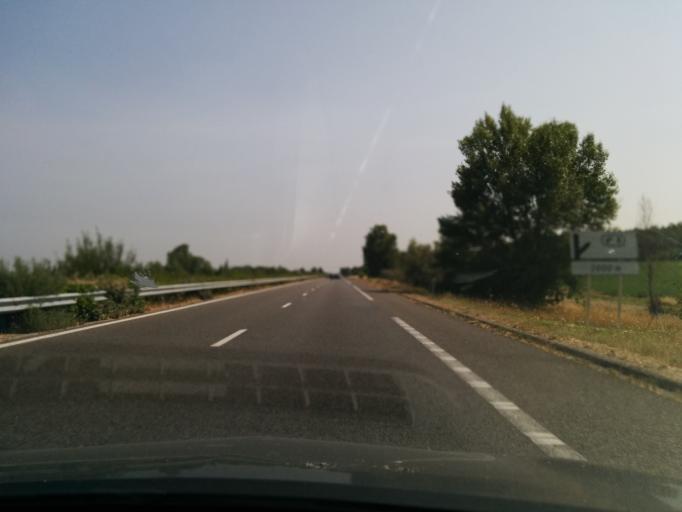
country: FR
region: Midi-Pyrenees
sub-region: Departement du Tarn
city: Lisle-sur-Tarn
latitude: 43.8278
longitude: 1.8243
